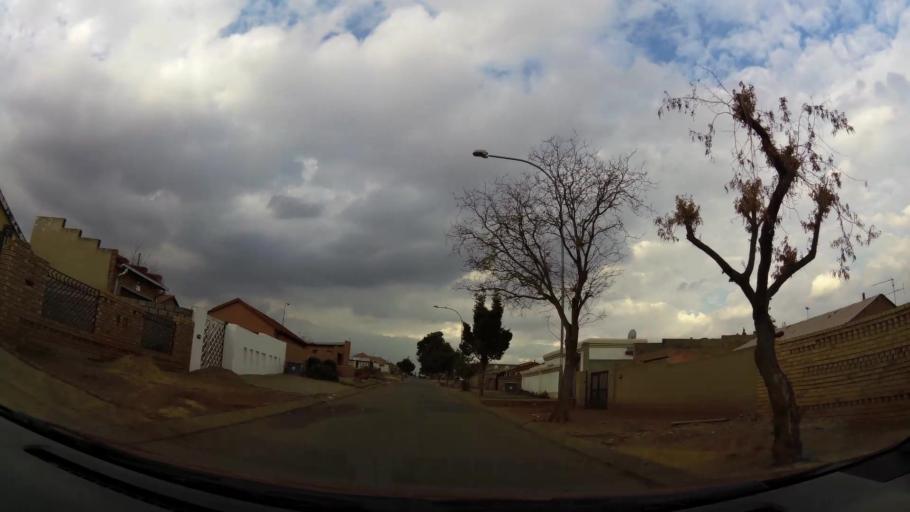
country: ZA
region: Gauteng
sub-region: City of Johannesburg Metropolitan Municipality
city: Soweto
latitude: -26.2451
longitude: 27.8132
